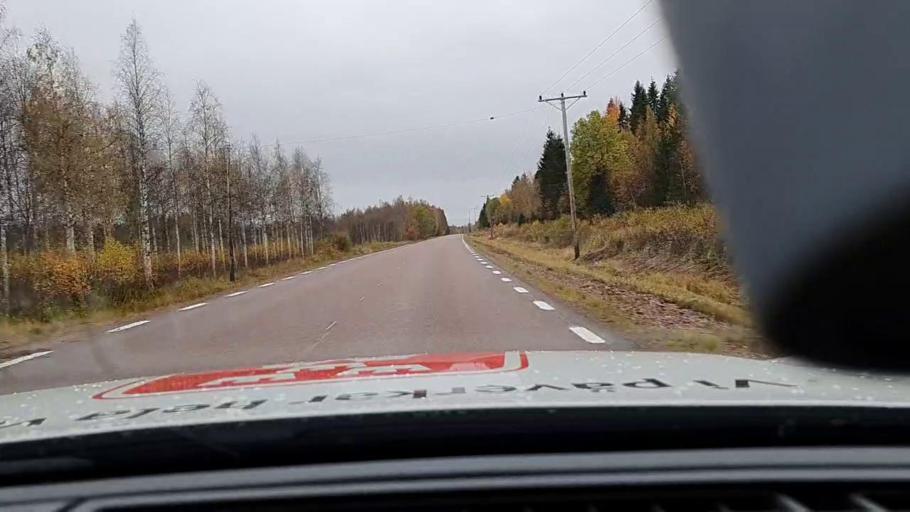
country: FI
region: Lapland
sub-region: Torniolaakso
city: Ylitornio
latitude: 66.1274
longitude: 23.9109
